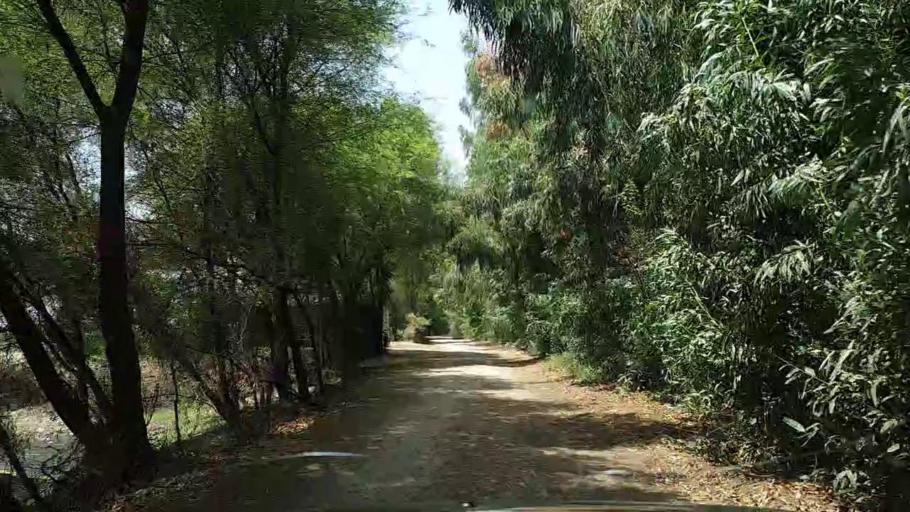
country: PK
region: Sindh
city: Ghotki
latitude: 28.0876
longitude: 69.3109
